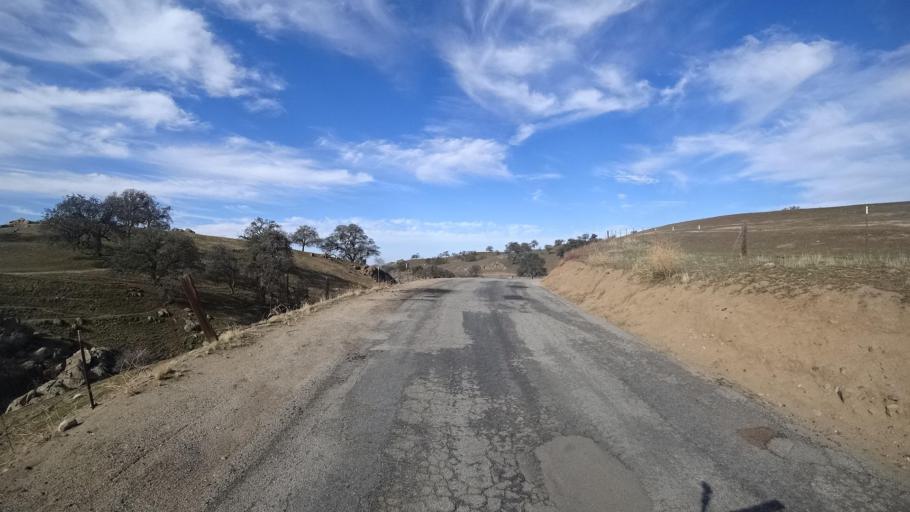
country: US
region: California
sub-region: Kern County
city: Oildale
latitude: 35.6141
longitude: -118.8418
